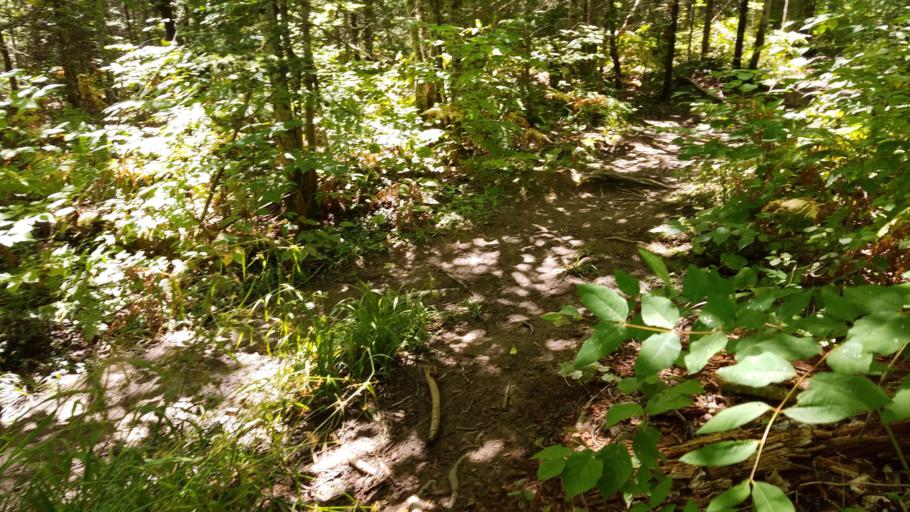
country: US
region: Michigan
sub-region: Ontonagon County
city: Ontonagon
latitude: 46.6500
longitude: -89.1672
